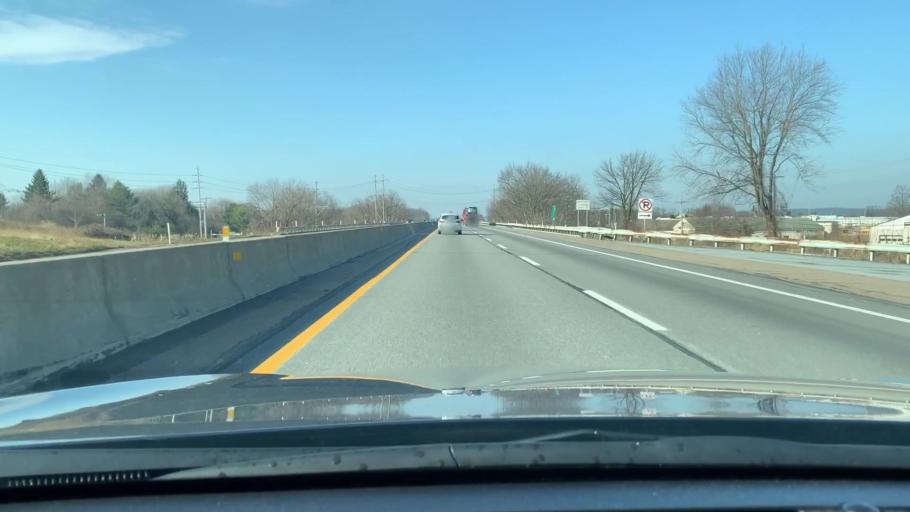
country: US
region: Pennsylvania
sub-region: Chester County
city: Chester Springs
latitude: 40.0703
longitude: -75.6772
